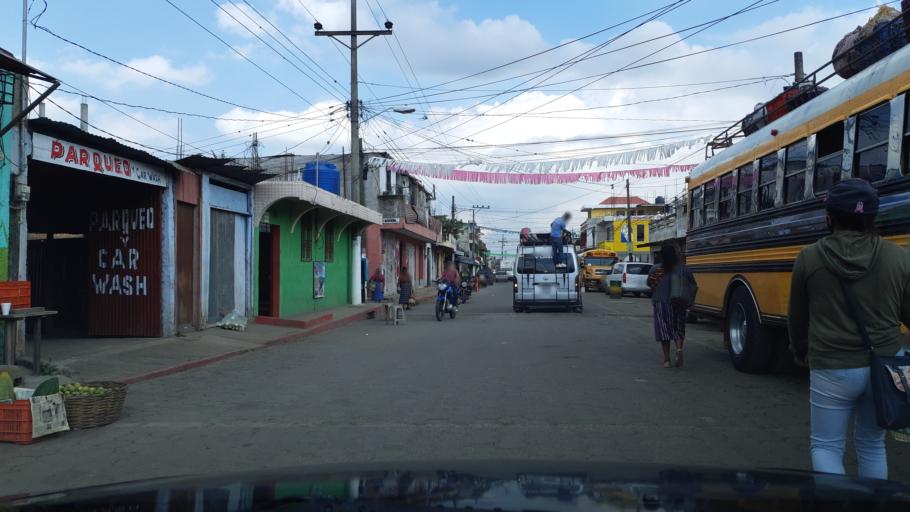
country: GT
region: Chimaltenango
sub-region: Municipio de Chimaltenango
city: Chimaltenango
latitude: 14.6674
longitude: -90.8134
